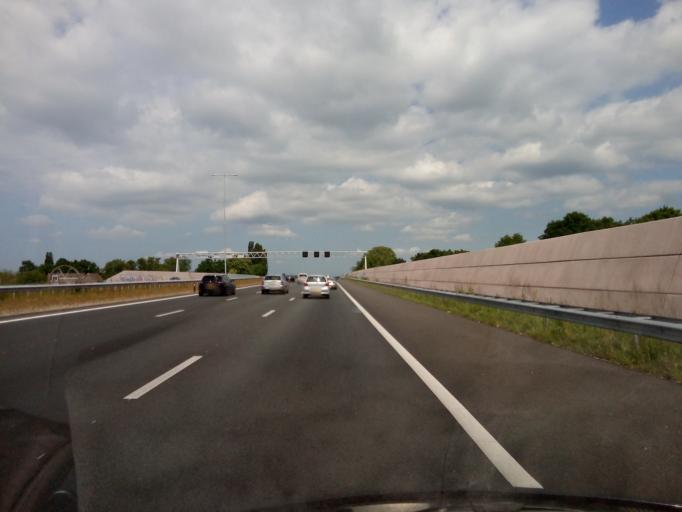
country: NL
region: Utrecht
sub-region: Gemeente De Bilt
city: De Bilt
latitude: 52.1560
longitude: 5.1671
